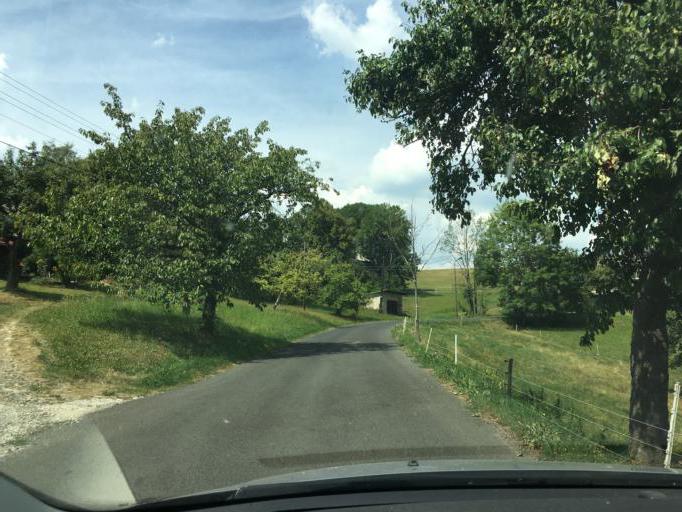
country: CZ
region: Liberecky
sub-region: Okres Semily
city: Ponikla
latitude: 50.6780
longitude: 15.4863
